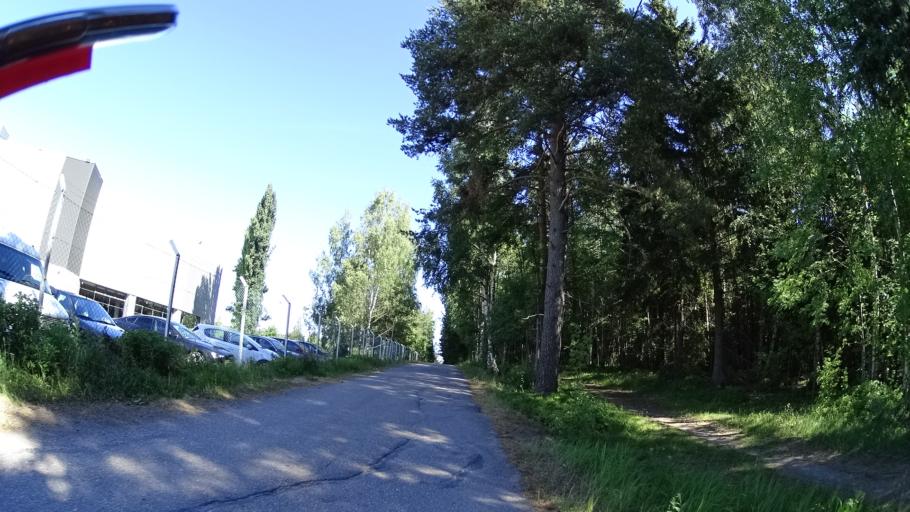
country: FI
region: Uusimaa
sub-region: Helsinki
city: Kilo
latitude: 60.2771
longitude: 24.8250
